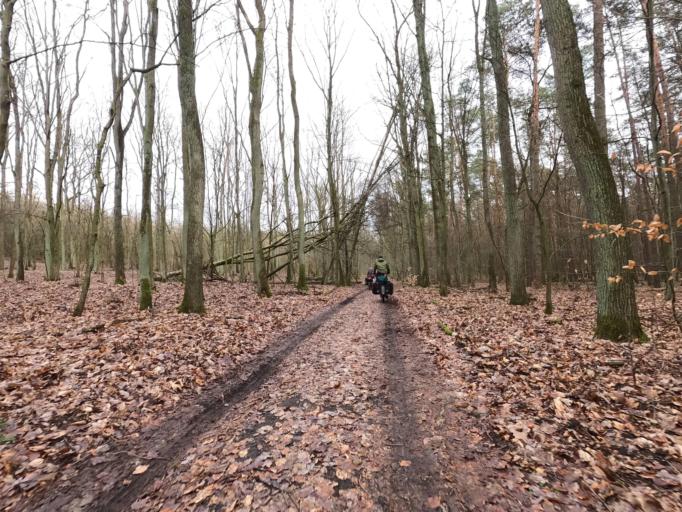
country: PL
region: Greater Poland Voivodeship
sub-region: Powiat pilski
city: Bialosliwie
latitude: 53.0956
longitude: 17.0943
